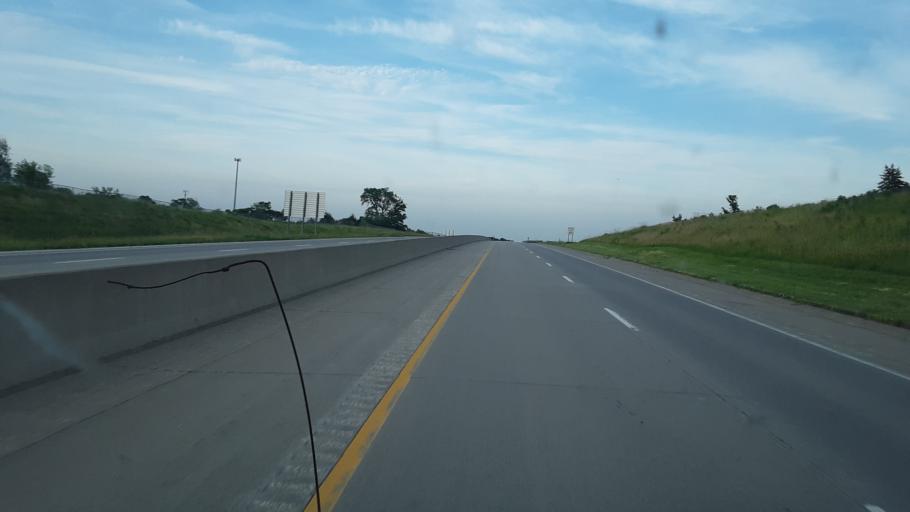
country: US
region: Iowa
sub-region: Tama County
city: Toledo
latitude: 41.9823
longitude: -92.5776
